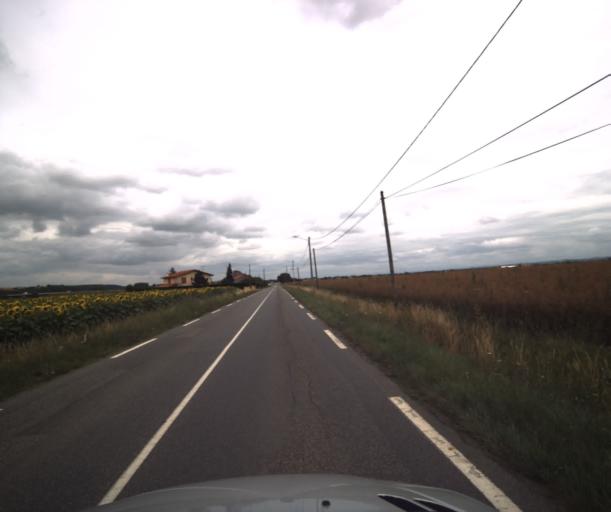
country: FR
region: Midi-Pyrenees
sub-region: Departement de la Haute-Garonne
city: Labarthe-sur-Leze
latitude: 43.4492
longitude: 1.4090
